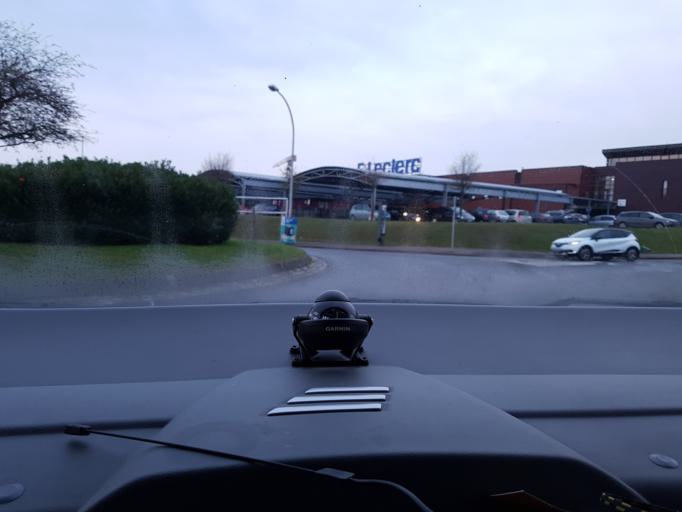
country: FR
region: Haute-Normandie
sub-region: Departement de la Seine-Maritime
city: Sainte-Marie-des-Champs
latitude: 49.6125
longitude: 0.7750
